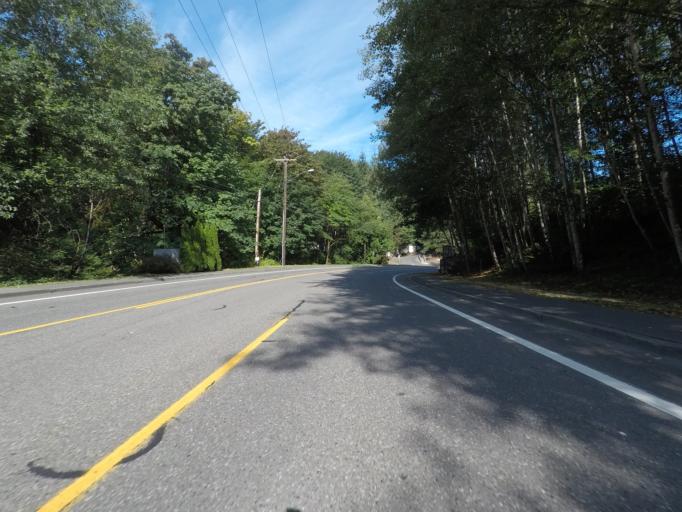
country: US
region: Washington
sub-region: King County
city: Bothell
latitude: 47.7416
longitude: -122.2104
